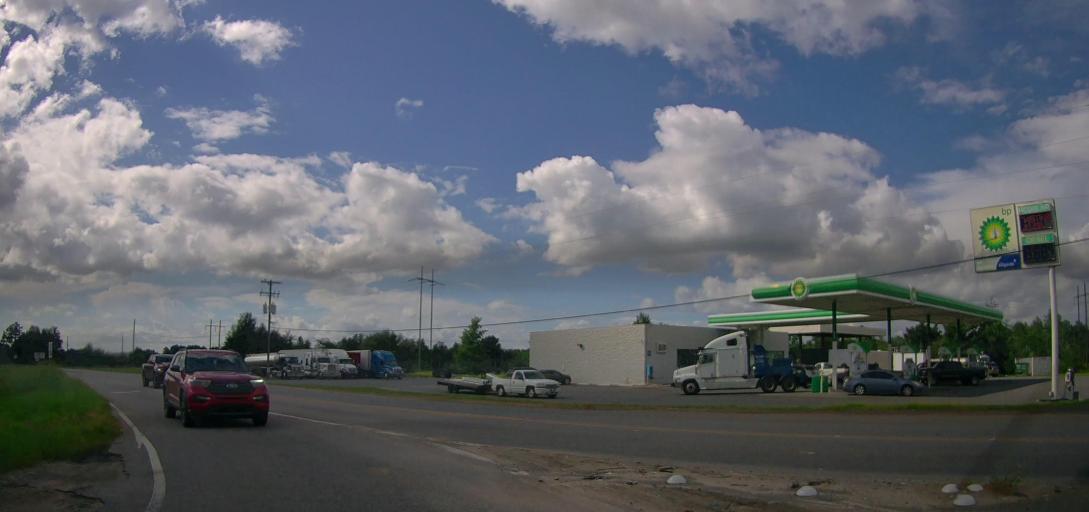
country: US
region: Georgia
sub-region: Coffee County
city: Douglas
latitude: 31.5385
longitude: -82.8107
